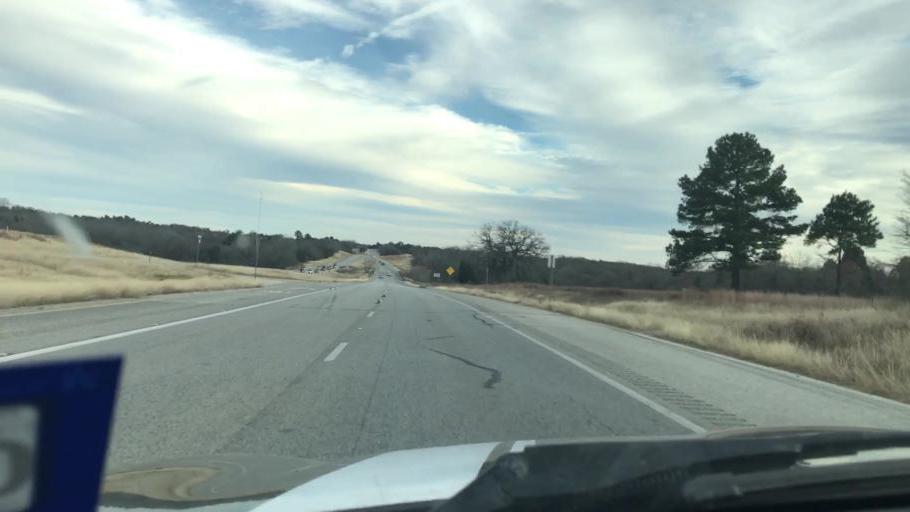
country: US
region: Texas
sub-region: Bastrop County
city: Elgin
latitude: 30.3067
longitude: -97.3007
